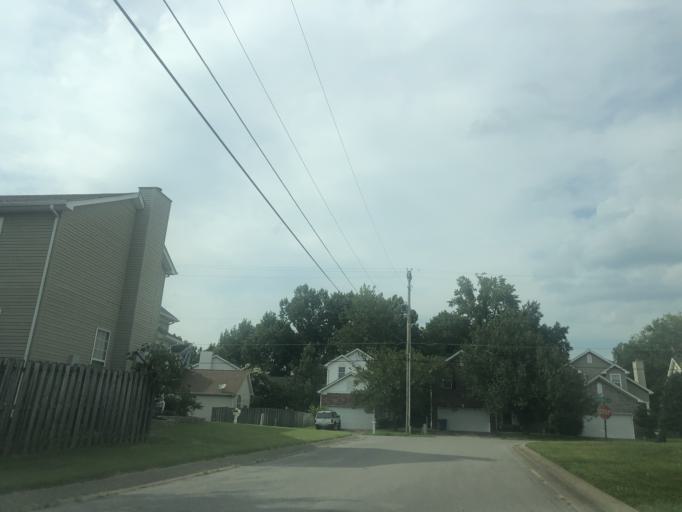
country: US
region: Tennessee
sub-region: Wilson County
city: Green Hill
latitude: 36.1849
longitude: -86.5849
